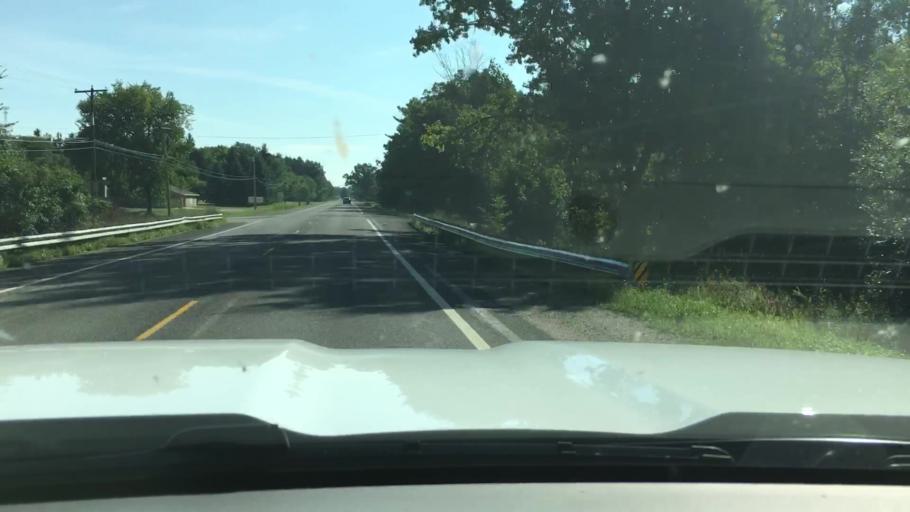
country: US
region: Michigan
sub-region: Montcalm County
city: Edmore
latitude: 43.4061
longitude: -84.9658
